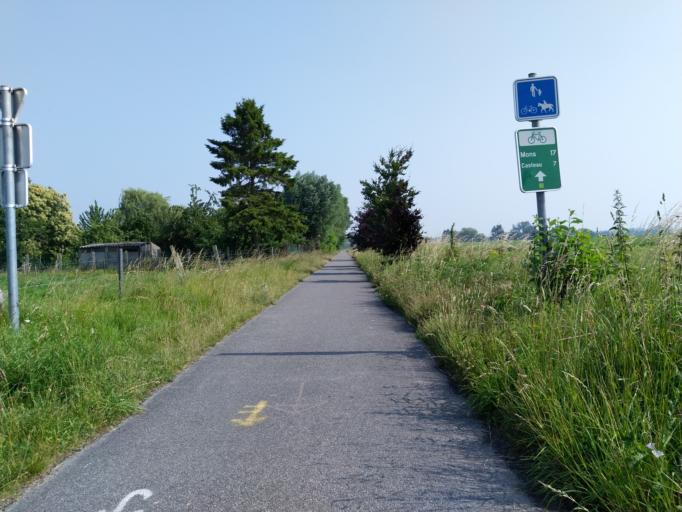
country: BE
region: Wallonia
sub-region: Province du Hainaut
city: Soignies
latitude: 50.5604
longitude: 4.0032
